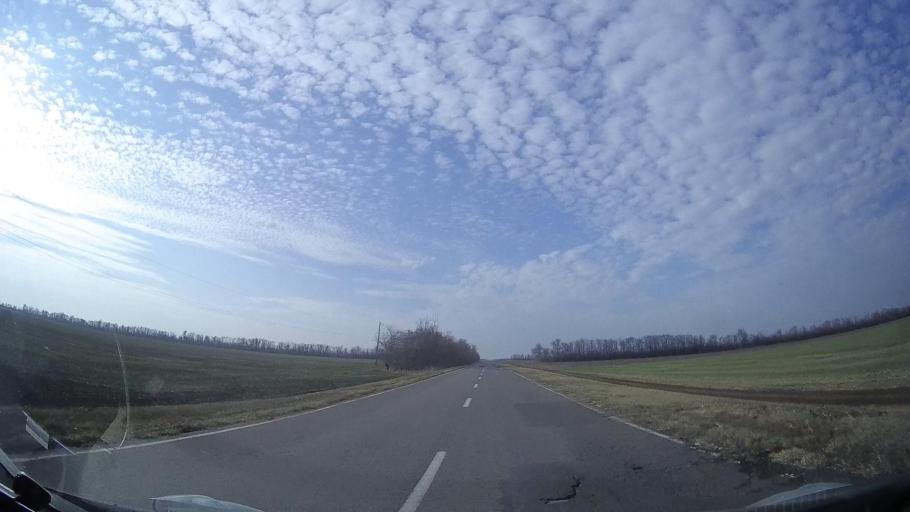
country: RU
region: Rostov
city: Veselyy
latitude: 46.9697
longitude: 40.7123
